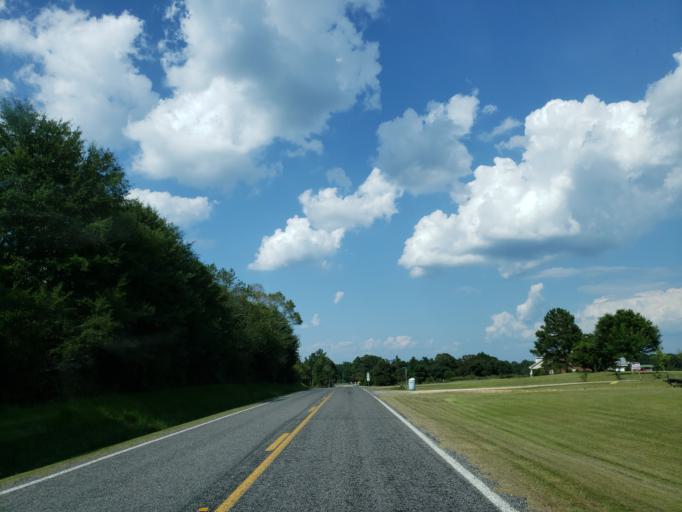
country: US
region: Mississippi
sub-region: Covington County
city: Collins
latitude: 31.6103
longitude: -89.4320
